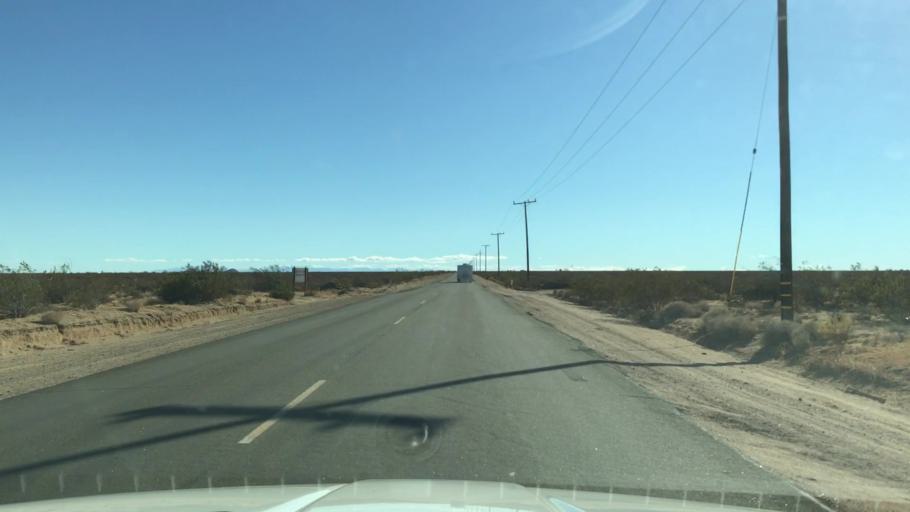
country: US
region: California
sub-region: Kern County
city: California City
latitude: 35.2331
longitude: -117.9859
